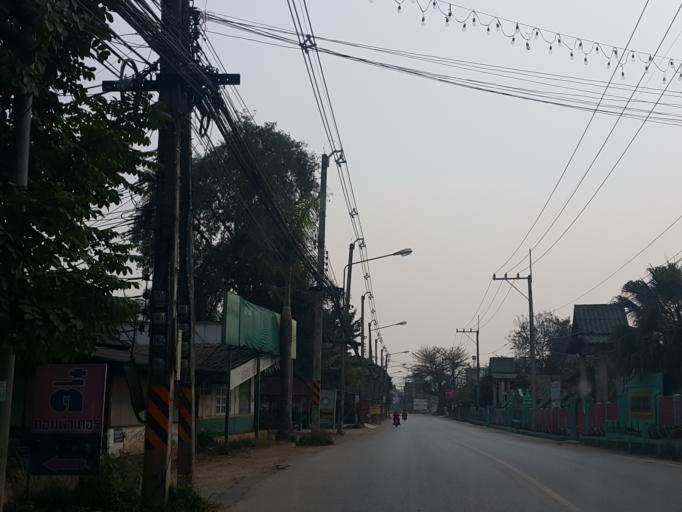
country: TH
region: Chiang Mai
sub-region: Amphoe Chiang Dao
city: Chiang Dao
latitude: 19.3649
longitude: 98.9646
